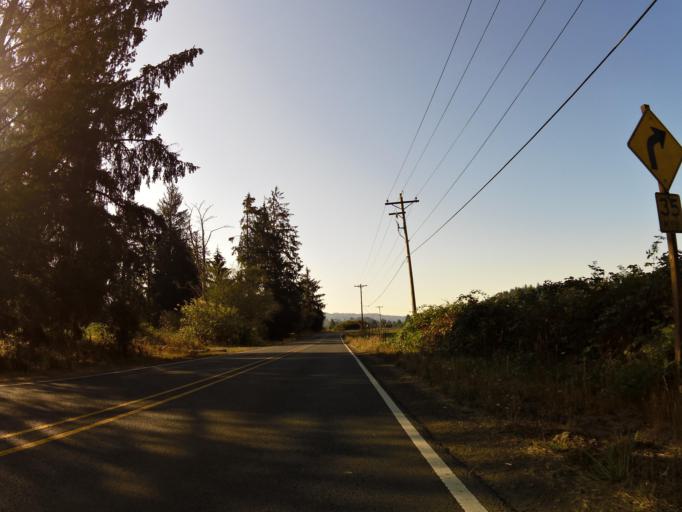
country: US
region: Oregon
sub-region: Tillamook County
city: Tillamook
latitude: 45.4291
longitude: -123.7778
